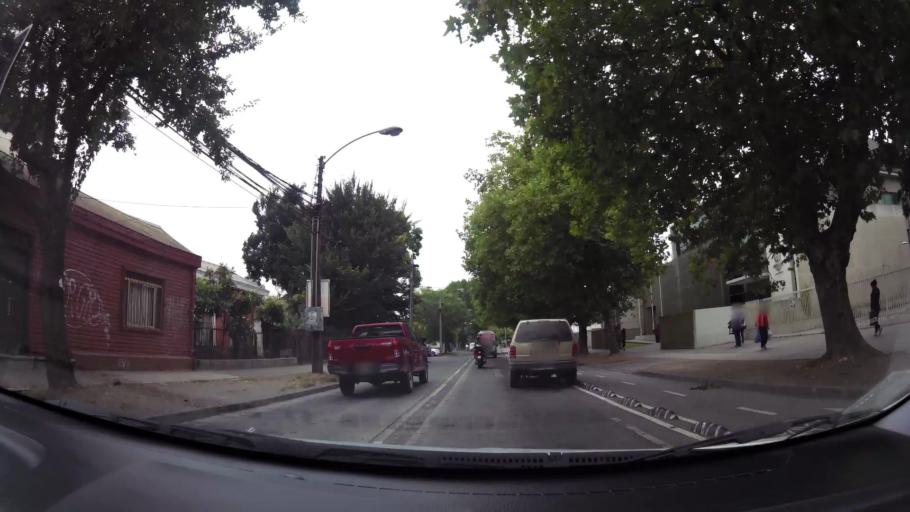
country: CL
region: Biobio
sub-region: Provincia de Concepcion
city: Concepcion
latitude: -36.8183
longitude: -73.0341
